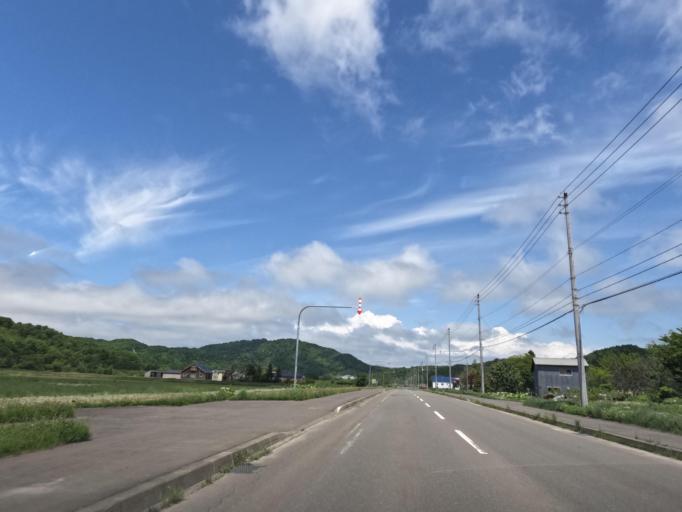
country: JP
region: Hokkaido
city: Tobetsu
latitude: 43.3013
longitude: 141.5494
